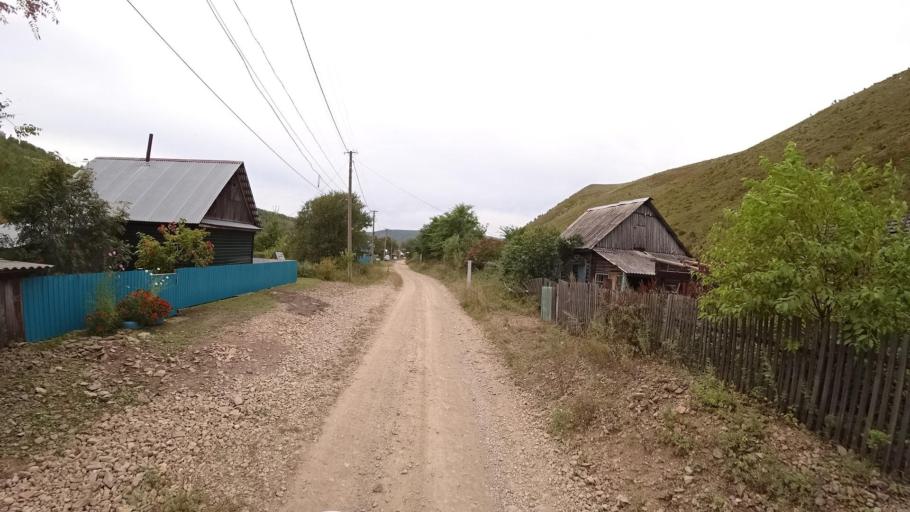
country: RU
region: Jewish Autonomous Oblast
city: Khingansk
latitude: 49.0250
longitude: 131.0723
